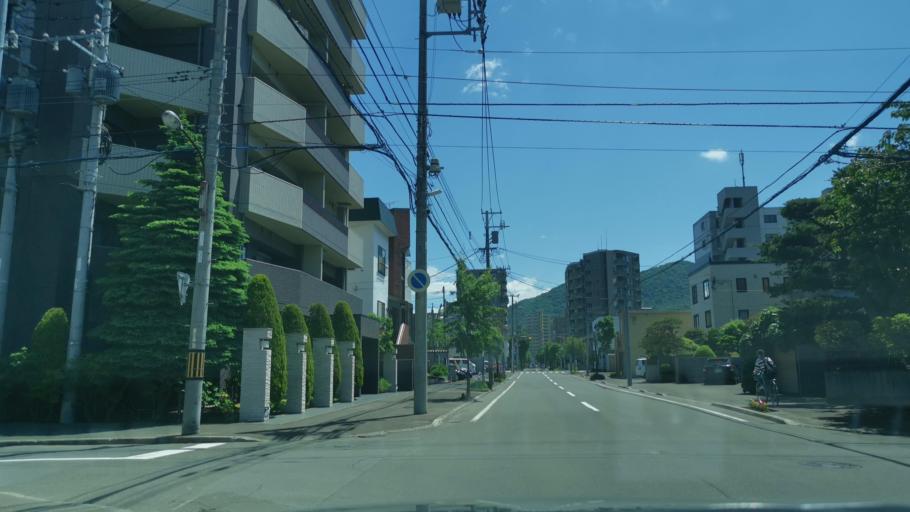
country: JP
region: Hokkaido
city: Sapporo
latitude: 43.0544
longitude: 141.3235
